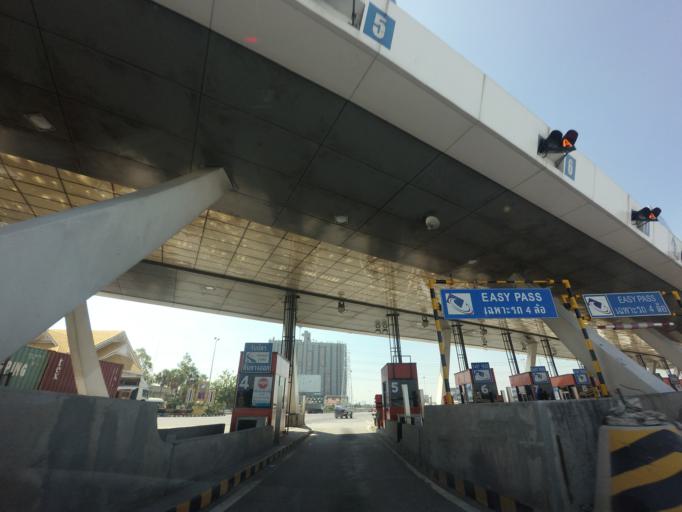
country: TH
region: Bangkok
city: Bang Na
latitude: 13.6429
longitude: 100.6826
